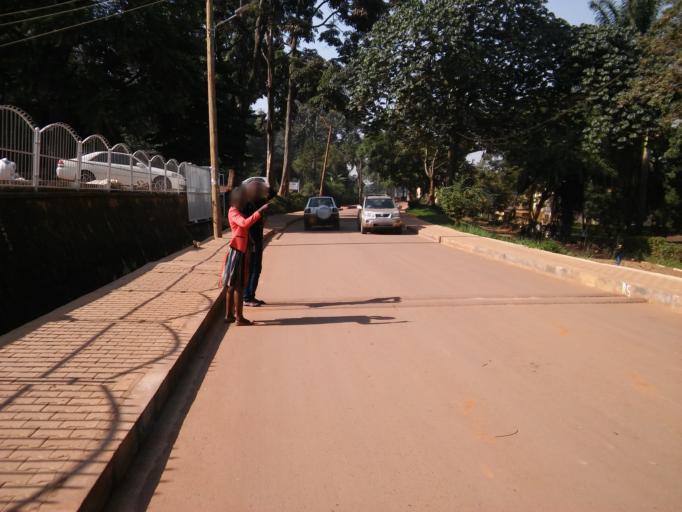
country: UG
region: Central Region
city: Kampala Central Division
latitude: 0.3324
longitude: 32.5664
